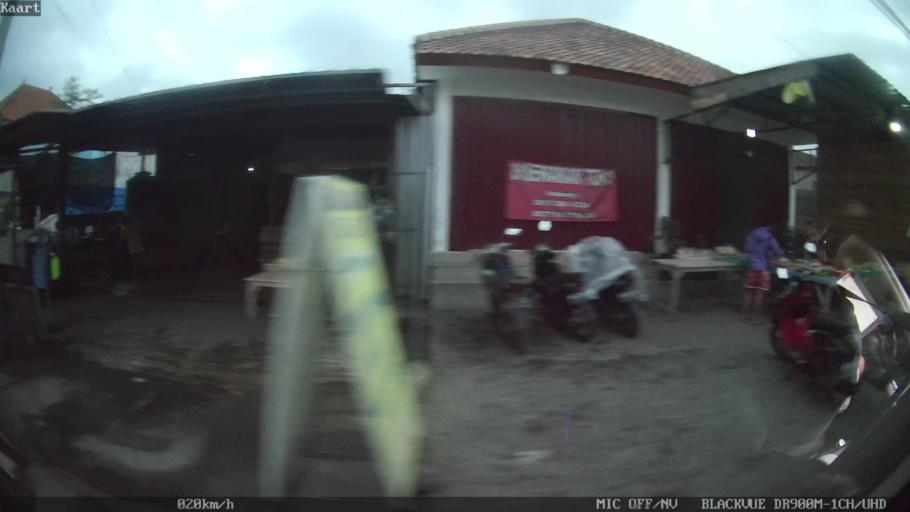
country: ID
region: Bali
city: Banjar Pasekan
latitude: -8.6256
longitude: 115.2707
